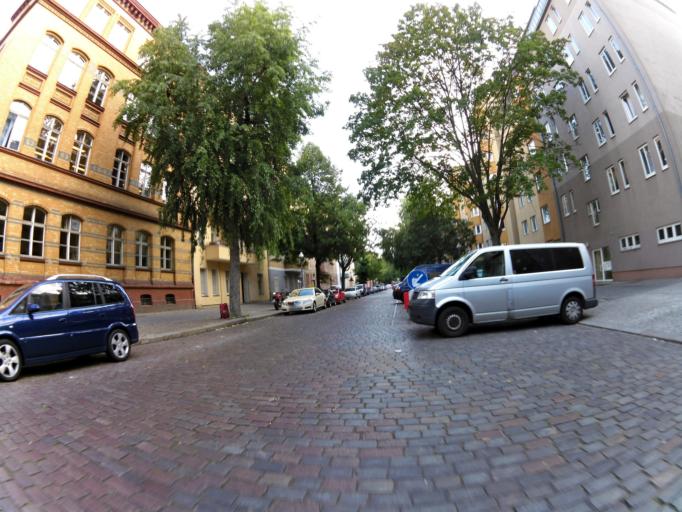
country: DE
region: Berlin
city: Wedding Bezirk
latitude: 52.5438
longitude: 13.3611
